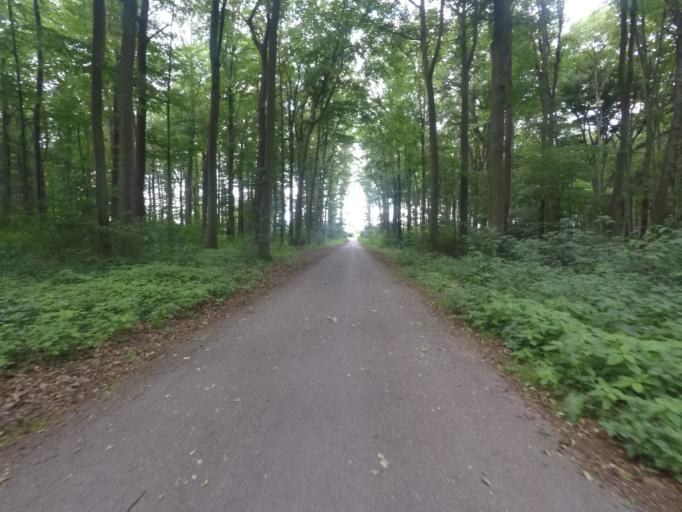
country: DE
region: North Rhine-Westphalia
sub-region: Regierungsbezirk Detmold
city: Hiddenhausen
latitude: 52.1724
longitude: 8.6018
